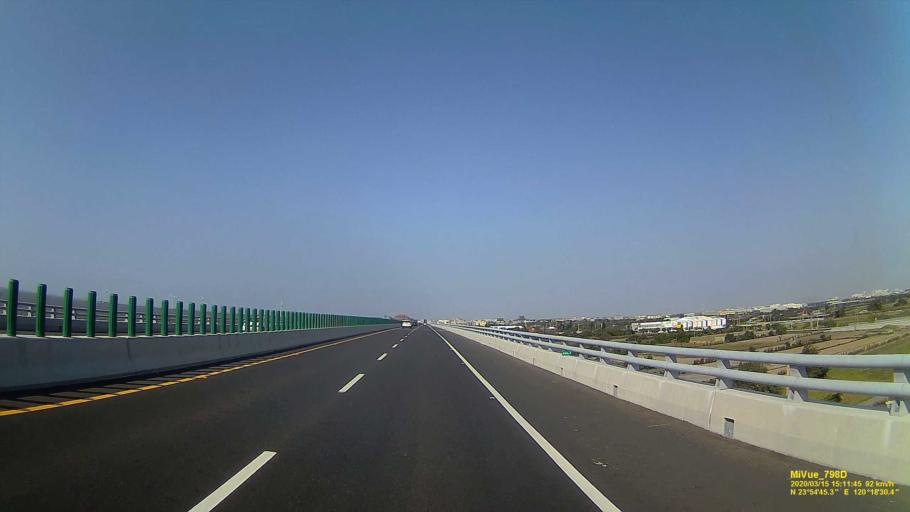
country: TW
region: Taiwan
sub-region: Changhua
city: Chang-hua
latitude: 23.9130
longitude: 120.3086
